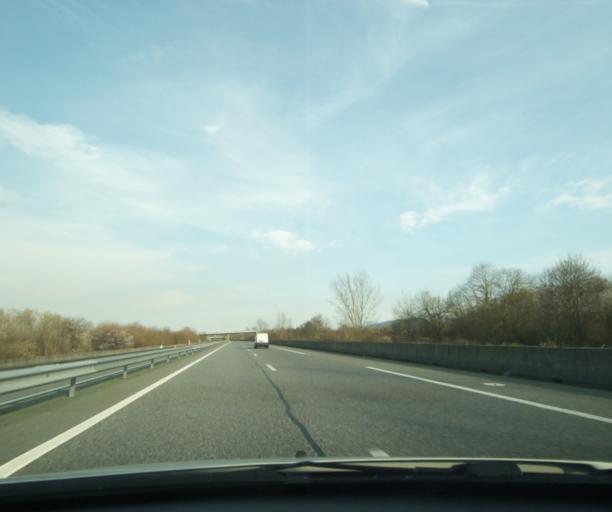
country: FR
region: Midi-Pyrenees
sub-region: Departement de la Haute-Garonne
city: Villeneuve-de-Riviere
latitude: 43.1143
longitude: 0.6626
